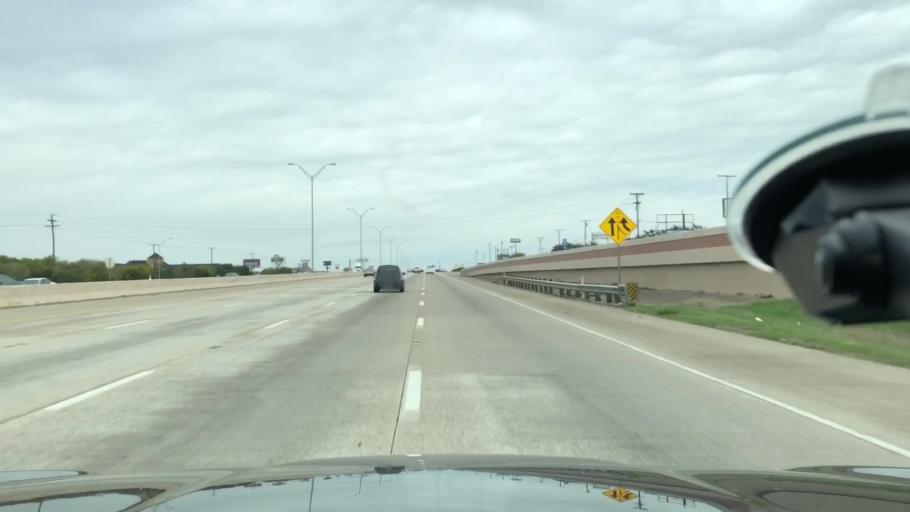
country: US
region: Texas
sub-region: Dallas County
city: DeSoto
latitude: 32.6134
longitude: -96.8229
